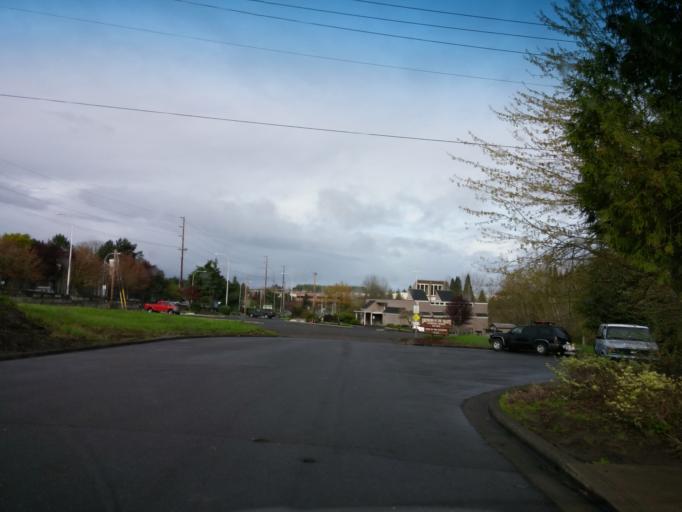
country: US
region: Oregon
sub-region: Washington County
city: Oak Hills
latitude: 45.5357
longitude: -122.8550
